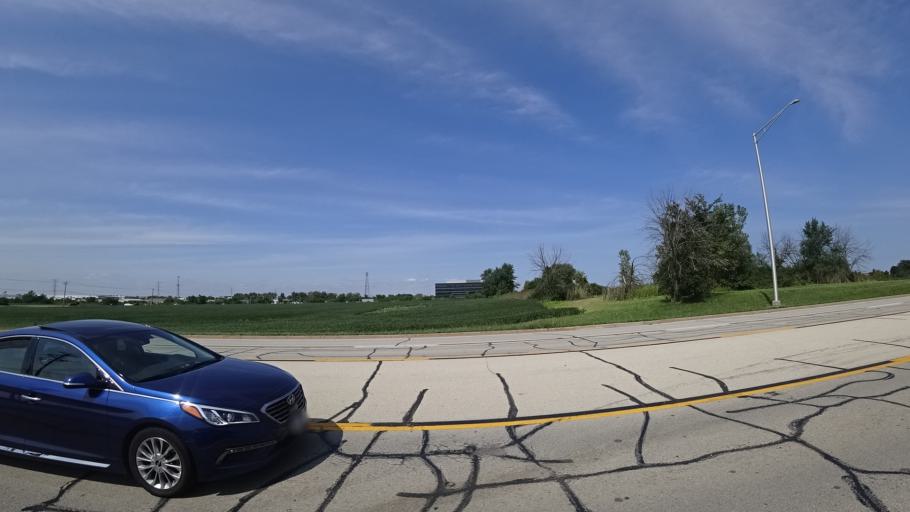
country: US
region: Illinois
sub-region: Will County
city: Frankfort Square
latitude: 41.5437
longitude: -87.8096
